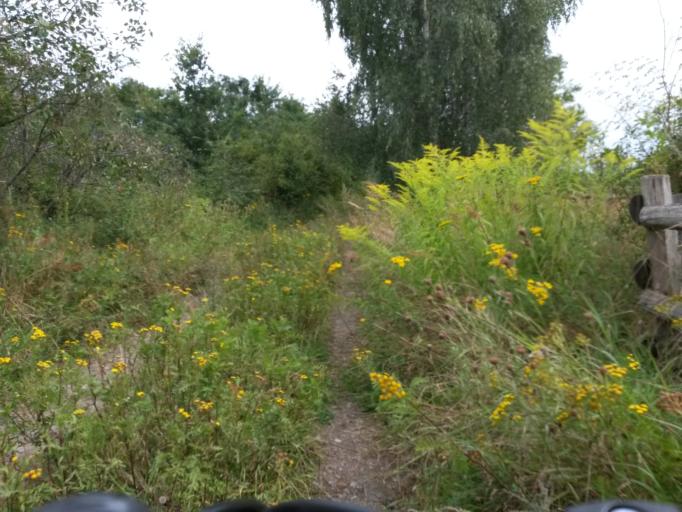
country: DE
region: Brandenburg
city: Angermunde
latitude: 53.0351
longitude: 13.9674
